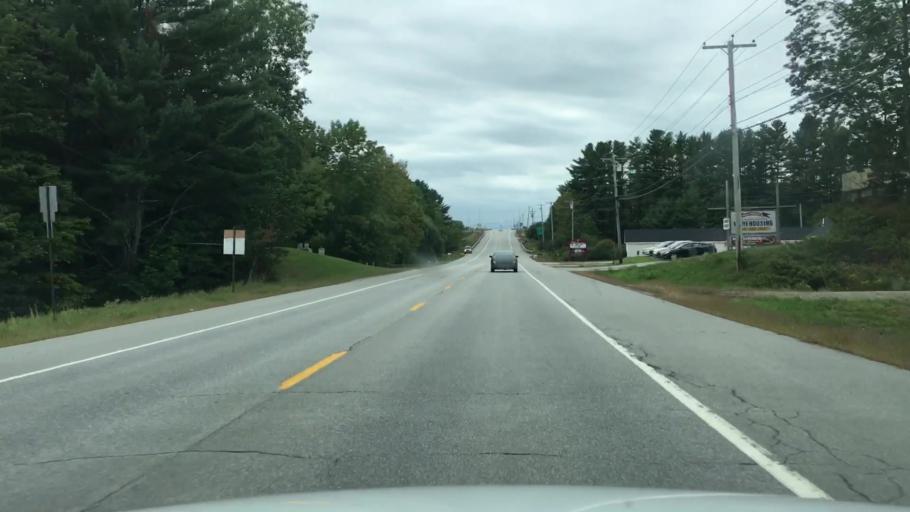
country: US
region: Maine
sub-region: Kennebec County
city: Gardiner
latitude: 44.2102
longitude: -69.8172
